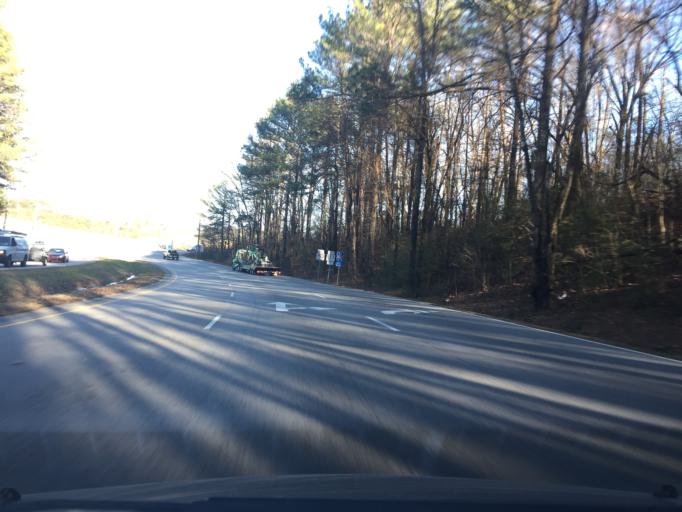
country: US
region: Tennessee
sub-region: Hamilton County
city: East Chattanooga
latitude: 35.0885
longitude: -85.2213
